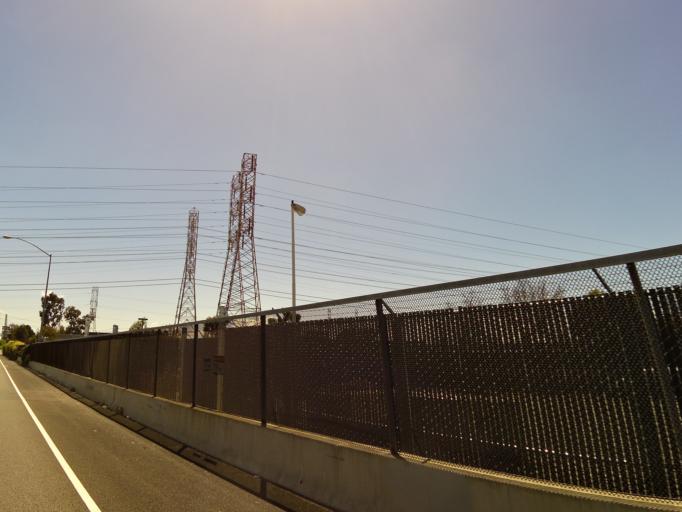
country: US
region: California
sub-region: Alameda County
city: Fremont
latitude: 37.5101
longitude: -121.9712
